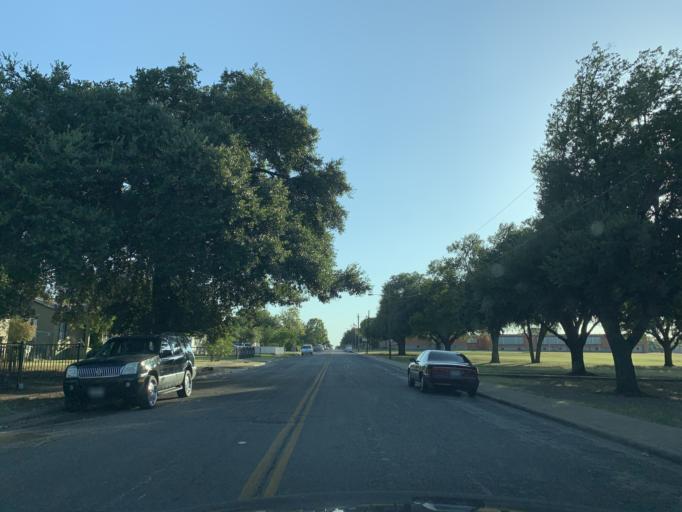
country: US
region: Texas
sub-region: Dallas County
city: Dallas
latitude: 32.7119
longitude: -96.7926
